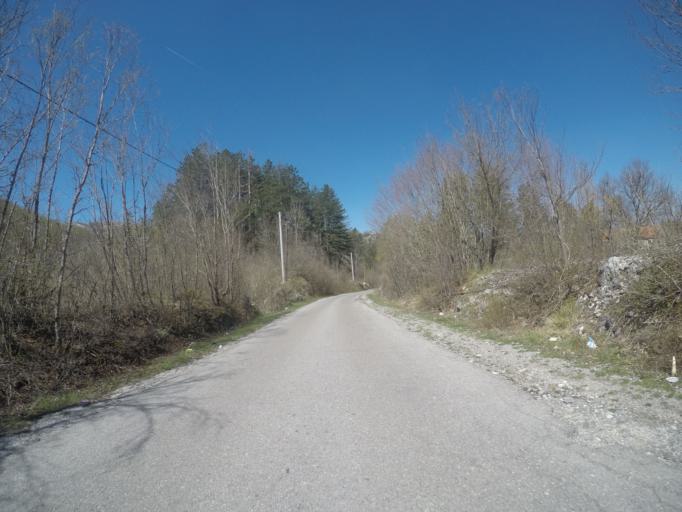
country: ME
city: Dobrota
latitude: 42.4670
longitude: 18.8577
